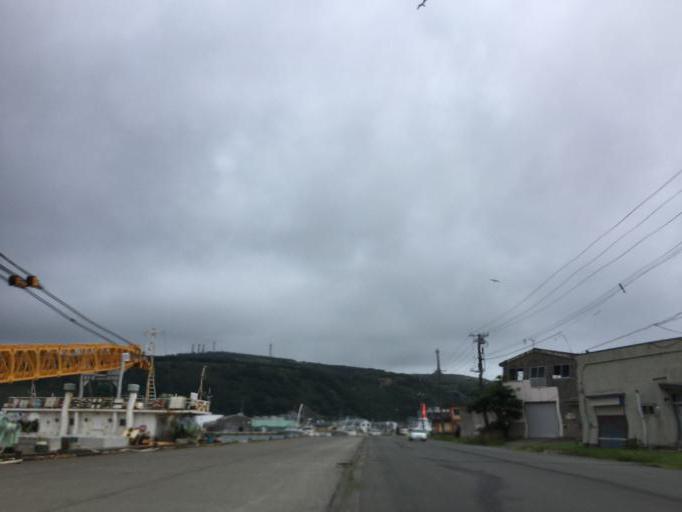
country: JP
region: Hokkaido
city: Wakkanai
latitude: 45.4045
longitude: 141.6818
